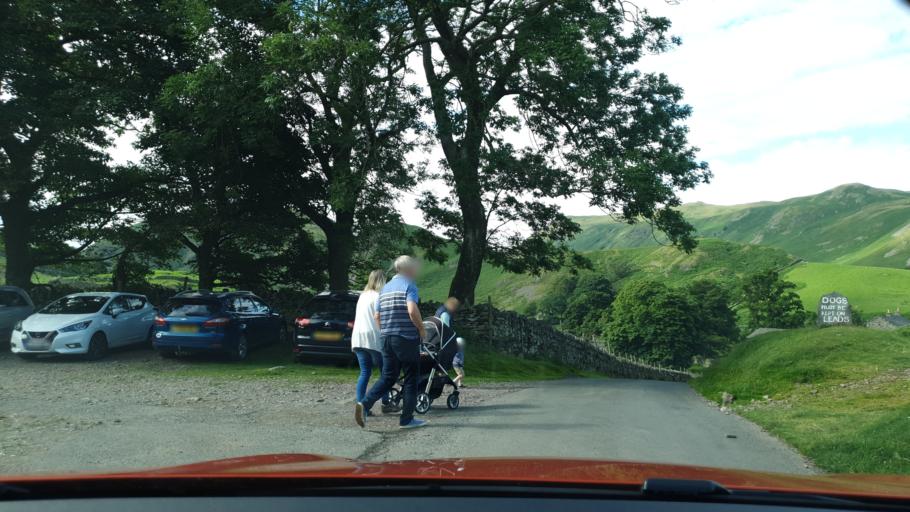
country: GB
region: England
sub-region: Cumbria
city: Penrith
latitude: 54.5647
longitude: -2.8744
